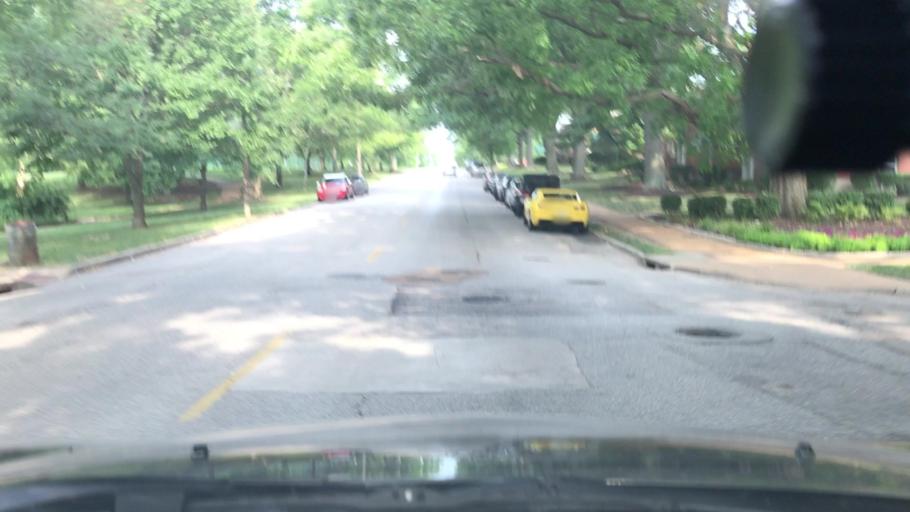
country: US
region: Missouri
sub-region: Saint Louis County
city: Maplewood
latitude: 38.6015
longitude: -90.2876
